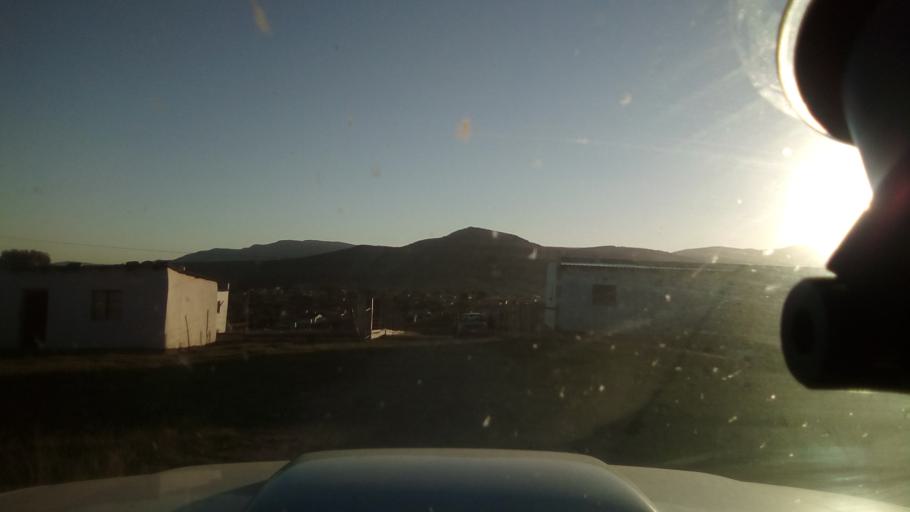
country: ZA
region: Eastern Cape
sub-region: Buffalo City Metropolitan Municipality
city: Bhisho
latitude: -32.7353
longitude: 27.3785
